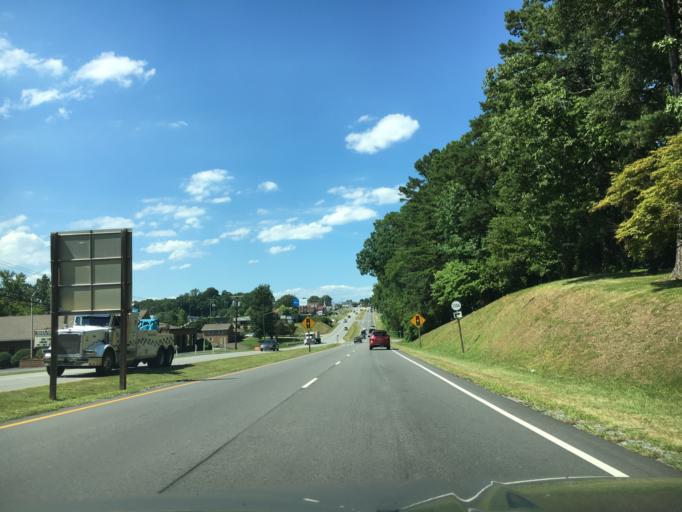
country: US
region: Virginia
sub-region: Halifax County
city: South Boston
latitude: 36.7273
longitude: -78.9188
